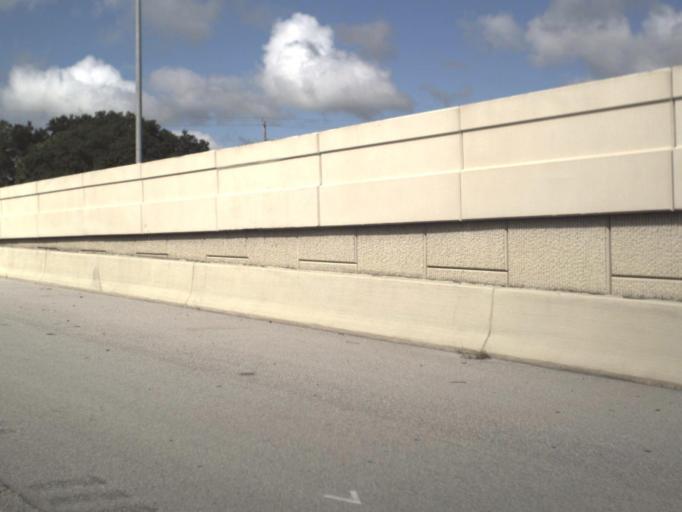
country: US
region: Florida
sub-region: Polk County
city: Winston
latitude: 28.0508
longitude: -82.0170
